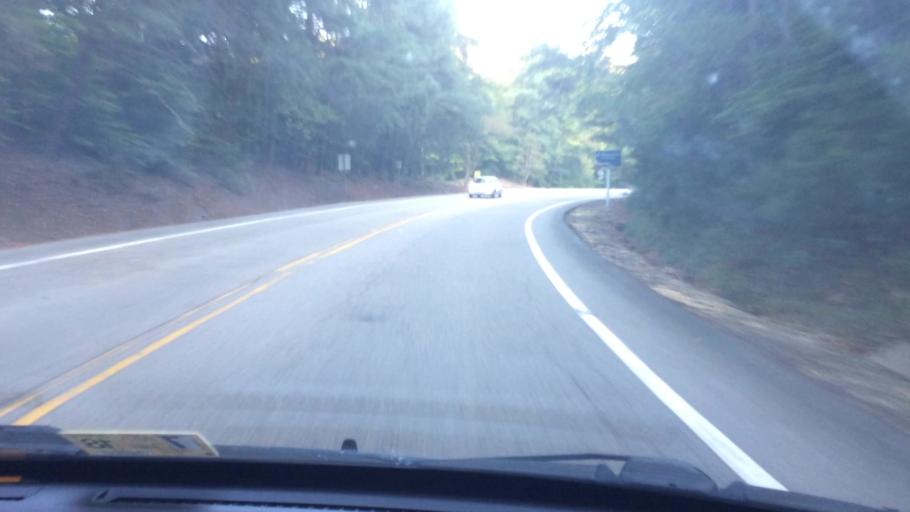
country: US
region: Virginia
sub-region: City of Williamsburg
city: Williamsburg
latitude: 37.2501
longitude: -76.7034
